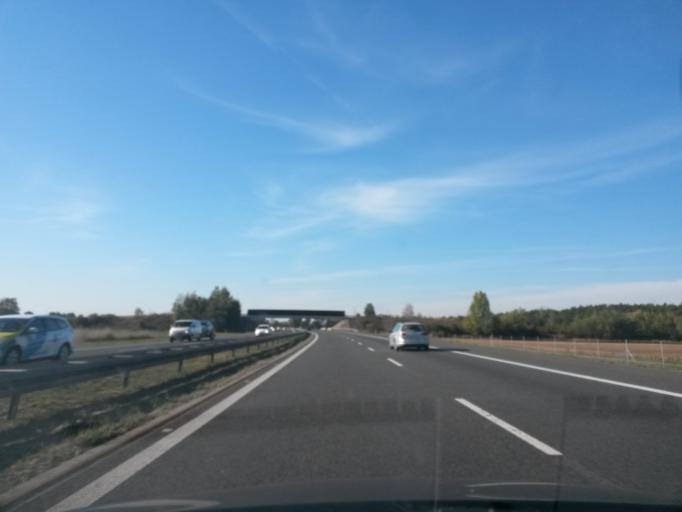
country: PL
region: Opole Voivodeship
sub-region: Powiat brzeski
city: Lewin Brzeski
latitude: 50.7050
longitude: 17.6136
